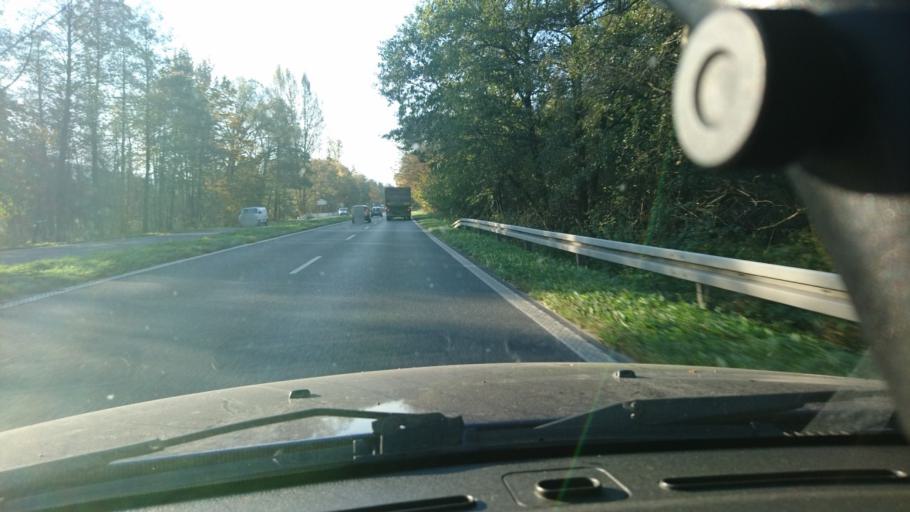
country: PL
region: Silesian Voivodeship
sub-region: Powiat cieszynski
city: Gorki Wielkie
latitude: 49.7681
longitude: 18.8091
